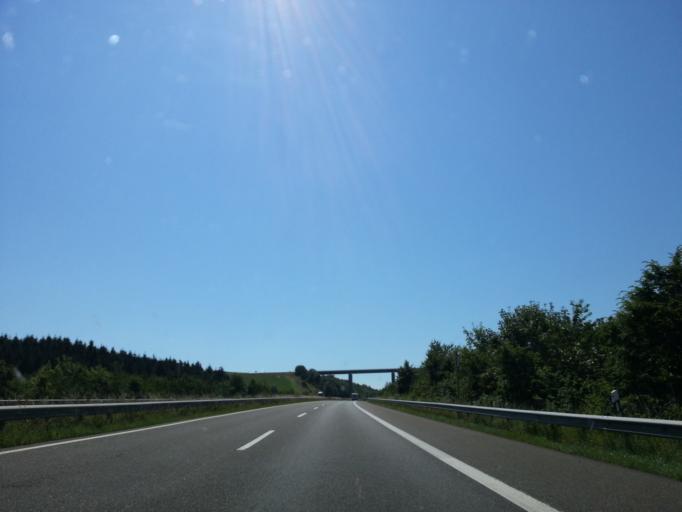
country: DE
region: Rheinland-Pfalz
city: Heisdorf
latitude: 50.1225
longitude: 6.4318
